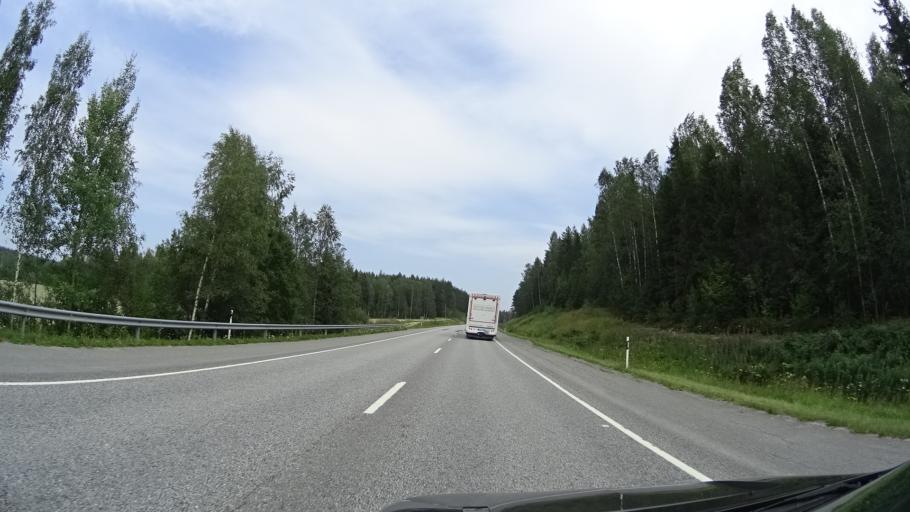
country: FI
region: Uusimaa
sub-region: Raaseporin
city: Karis
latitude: 60.0678
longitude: 23.8017
